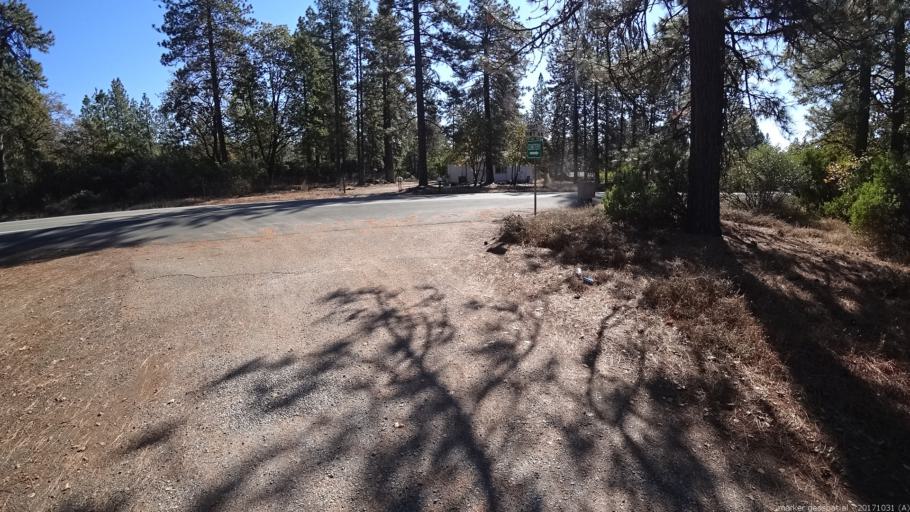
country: US
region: California
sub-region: Shasta County
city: Shingletown
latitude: 40.5081
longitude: -121.9602
